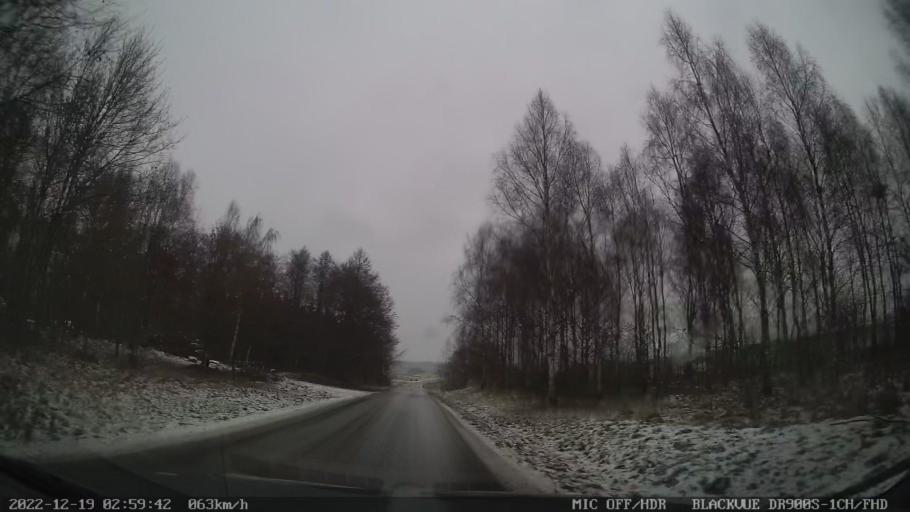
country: SE
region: Skane
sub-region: Tomelilla Kommun
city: Tomelilla
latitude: 55.5127
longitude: 14.0306
